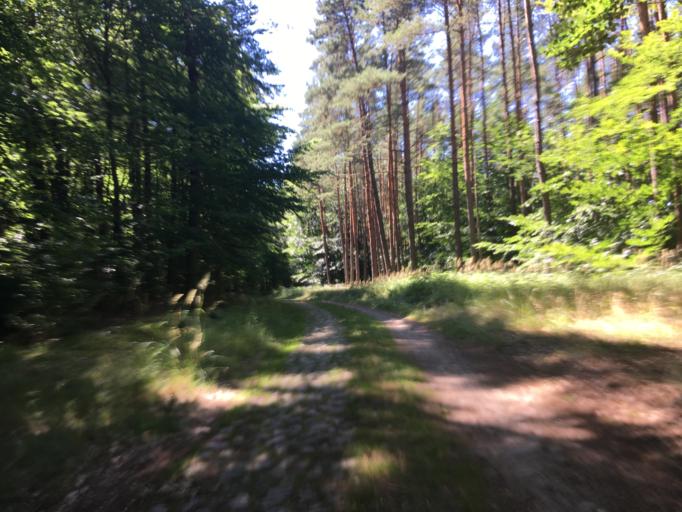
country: DE
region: Brandenburg
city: Grosswoltersdorf
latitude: 53.1304
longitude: 13.0145
